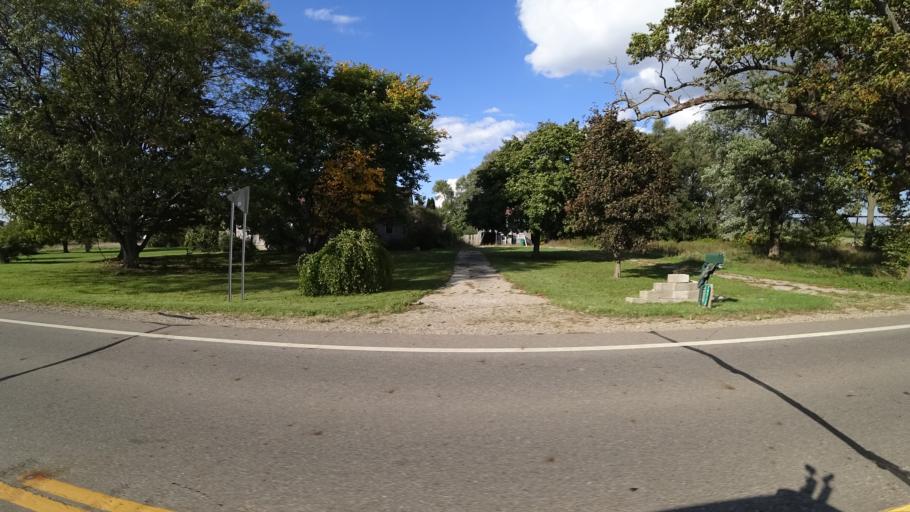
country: US
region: Michigan
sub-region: Saint Joseph County
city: Centreville
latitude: 41.9258
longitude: -85.5722
